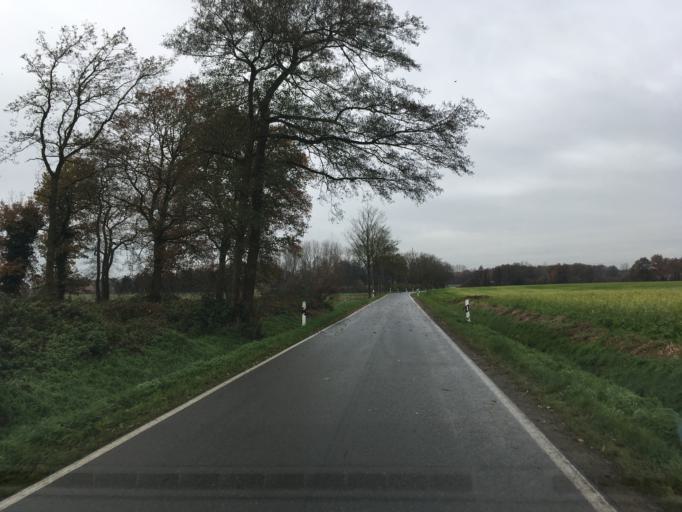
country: DE
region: North Rhine-Westphalia
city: Stadtlohn
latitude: 52.0105
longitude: 6.9552
